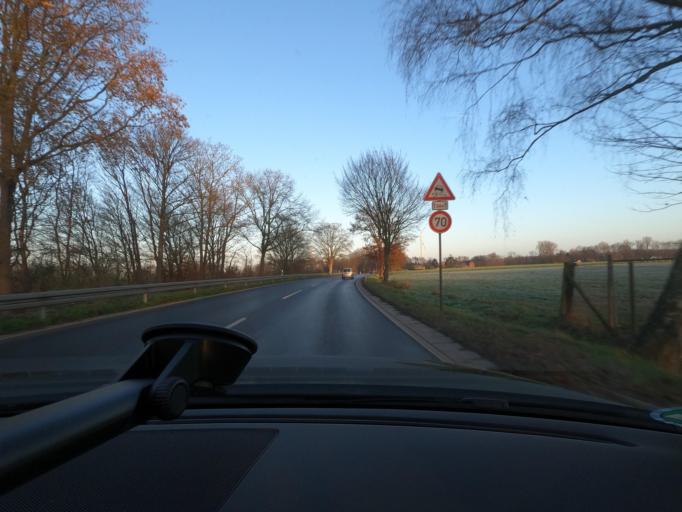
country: DE
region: North Rhine-Westphalia
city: Kempen
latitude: 51.3863
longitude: 6.3811
